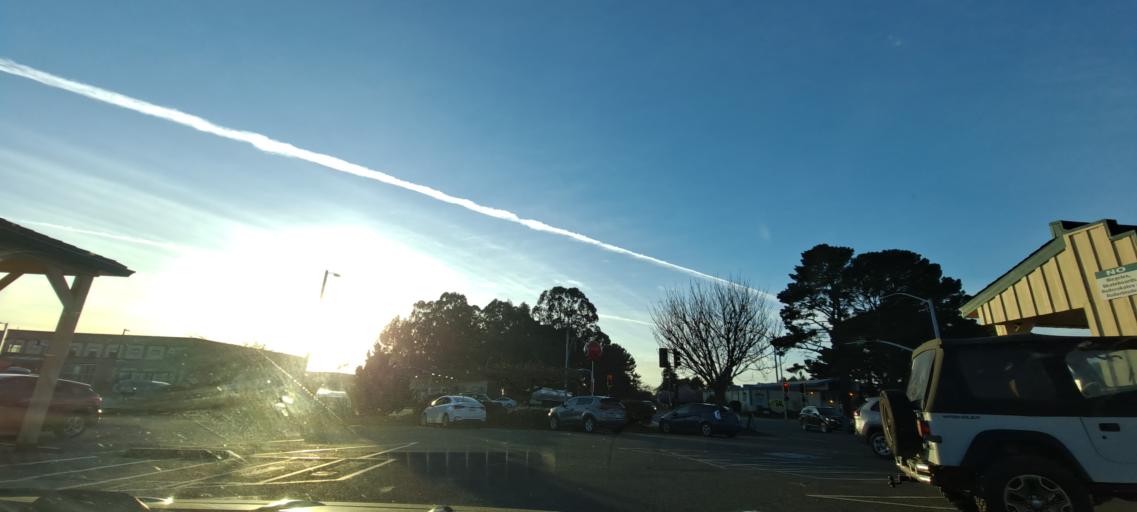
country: US
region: California
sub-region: Humboldt County
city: McKinleyville
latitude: 40.9420
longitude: -124.1005
